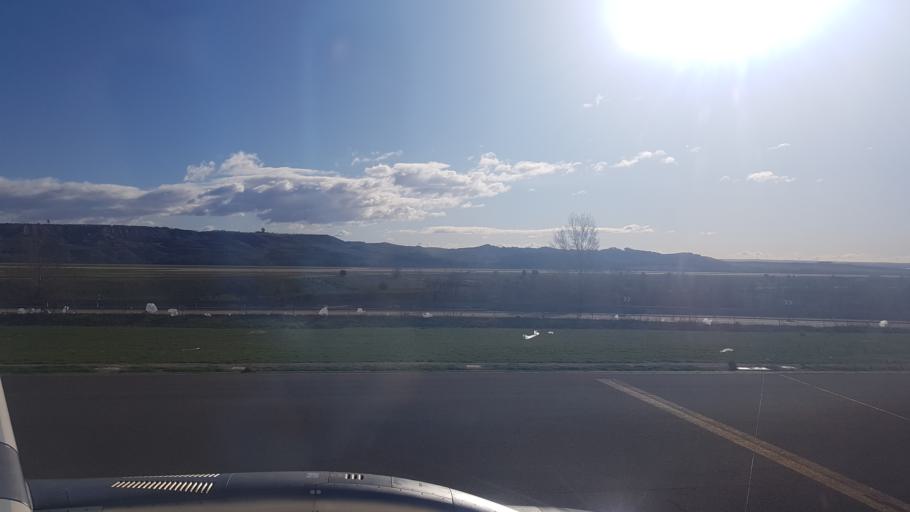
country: ES
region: Madrid
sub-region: Provincia de Madrid
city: Barajas de Madrid
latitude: 40.4886
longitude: -3.5611
